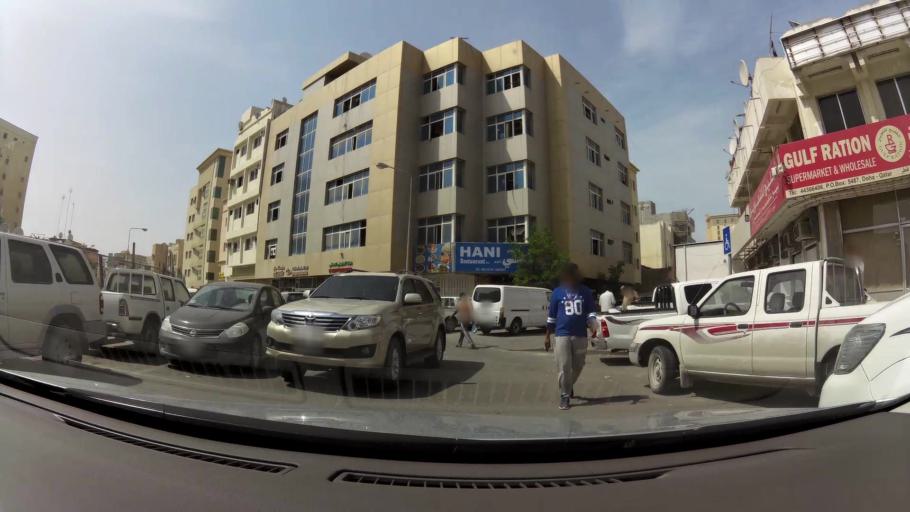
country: QA
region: Baladiyat ad Dawhah
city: Doha
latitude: 25.2792
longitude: 51.5427
